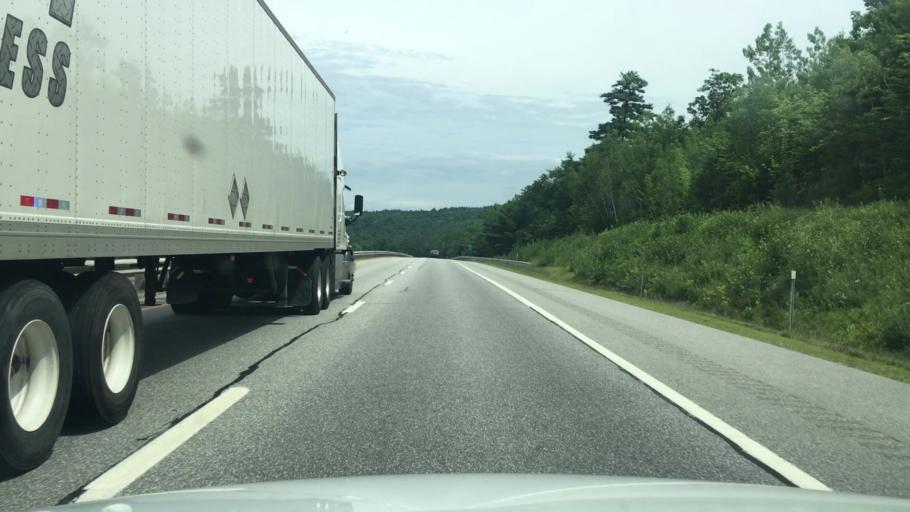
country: US
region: New Hampshire
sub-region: Grafton County
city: Ashland
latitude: 43.6385
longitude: -71.6492
